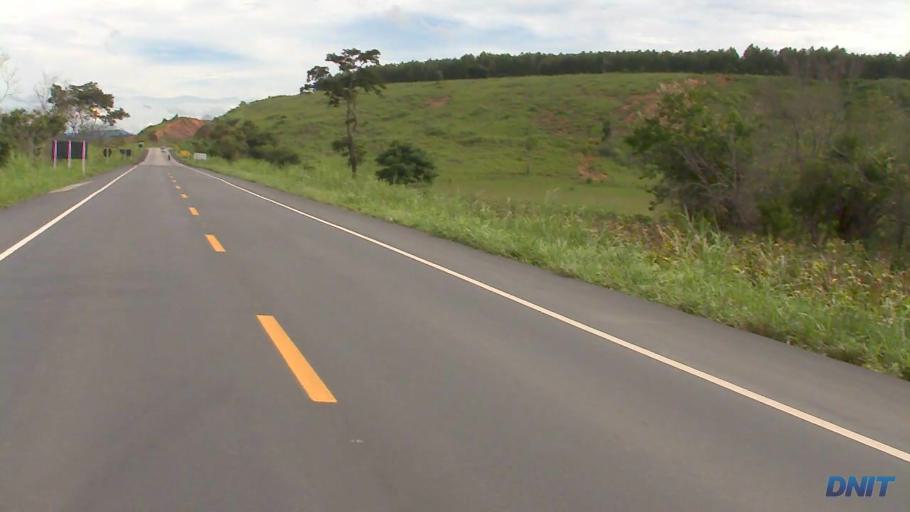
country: BR
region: Minas Gerais
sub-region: Ipaba
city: Ipaba
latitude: -19.2908
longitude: -42.3559
